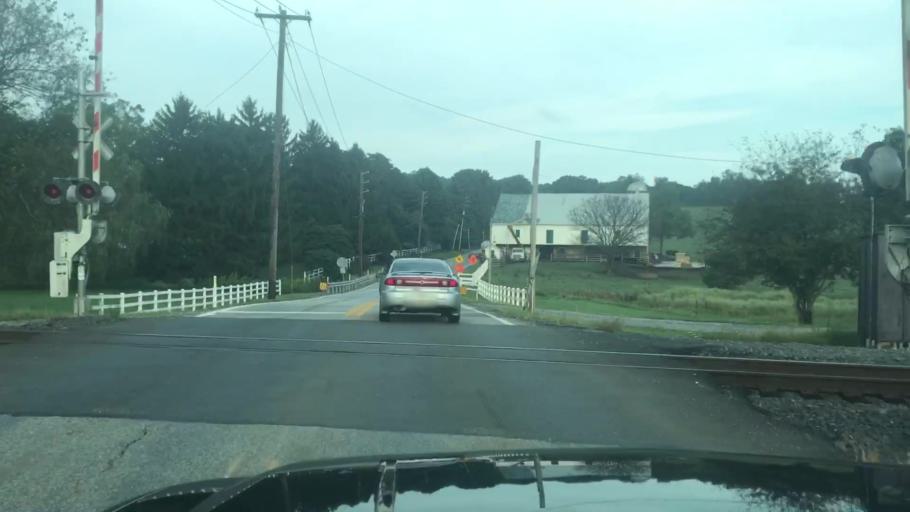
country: US
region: Pennsylvania
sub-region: Cumberland County
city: Shiremanstown
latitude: 40.1974
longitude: -76.9441
